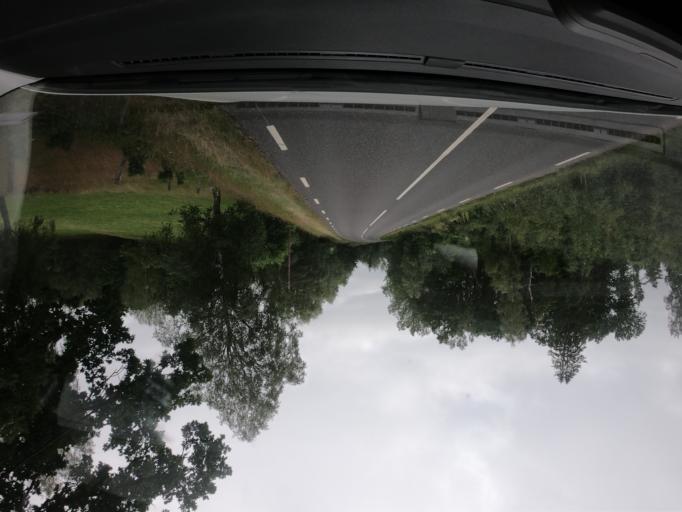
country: SE
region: Skane
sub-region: Perstorps Kommun
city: Perstorp
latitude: 56.0404
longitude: 13.3668
